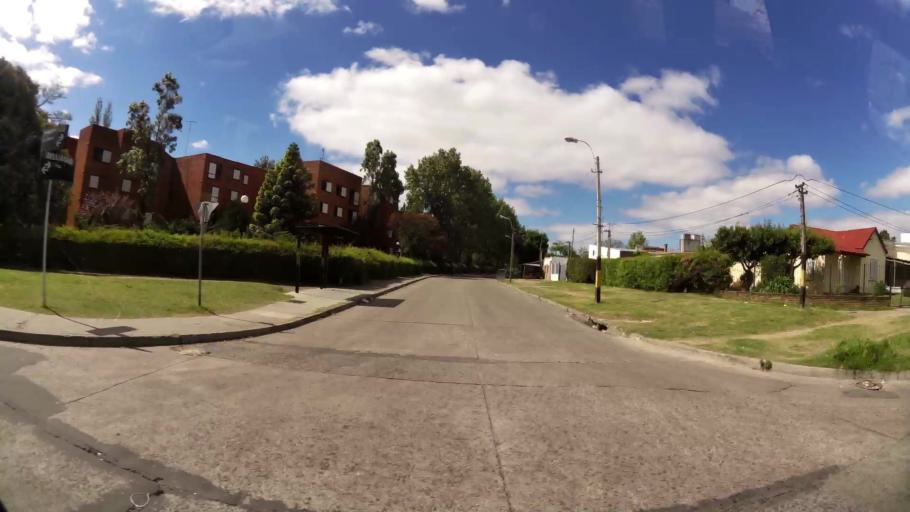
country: UY
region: Canelones
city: Paso de Carrasco
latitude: -34.8727
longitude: -56.1226
